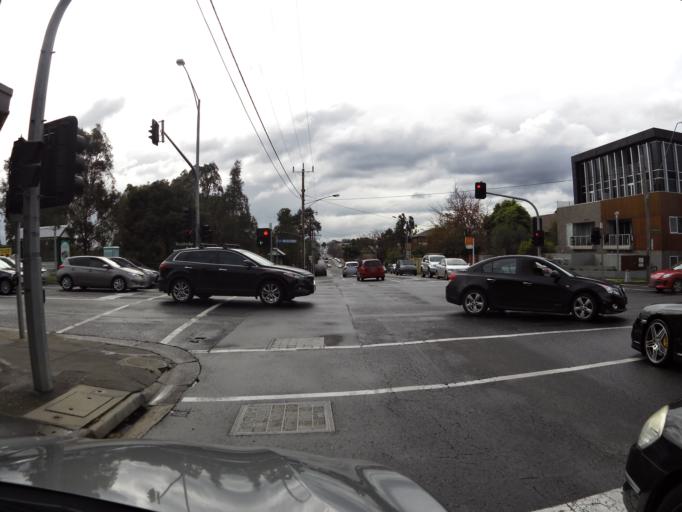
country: AU
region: Victoria
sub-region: Boroondara
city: Kew East
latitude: -37.8009
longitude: 145.0625
